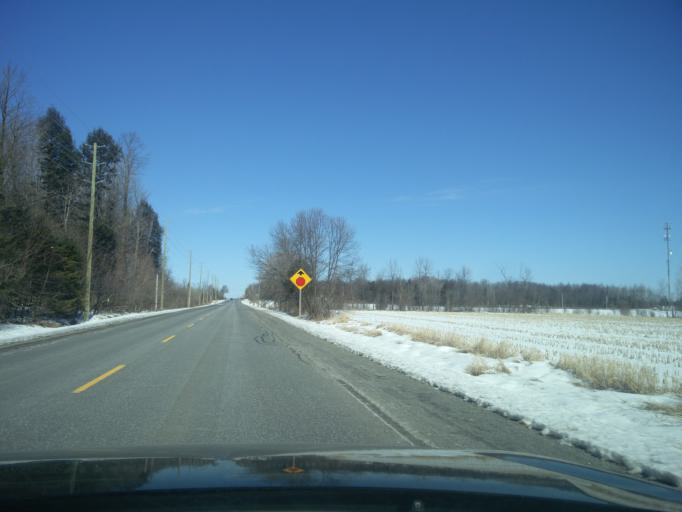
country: CA
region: Ontario
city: Bells Corners
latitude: 45.2325
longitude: -75.7239
